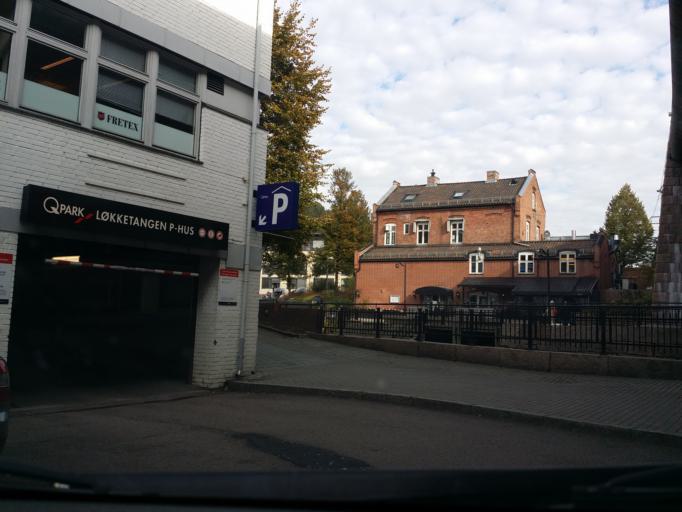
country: NO
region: Akershus
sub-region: Baerum
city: Sandvika
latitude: 59.8918
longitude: 10.5222
